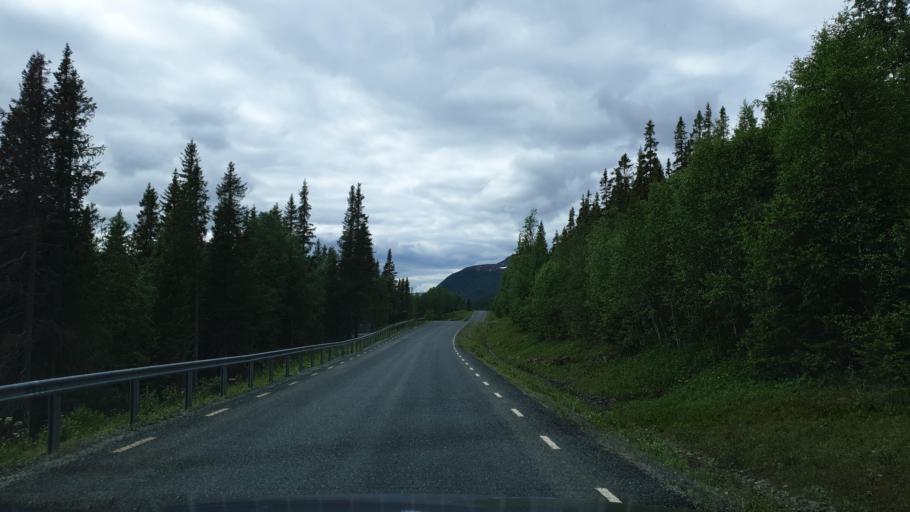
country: NO
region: Nordland
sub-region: Hattfjelldal
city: Hattfjelldal
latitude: 65.4433
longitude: 14.5425
